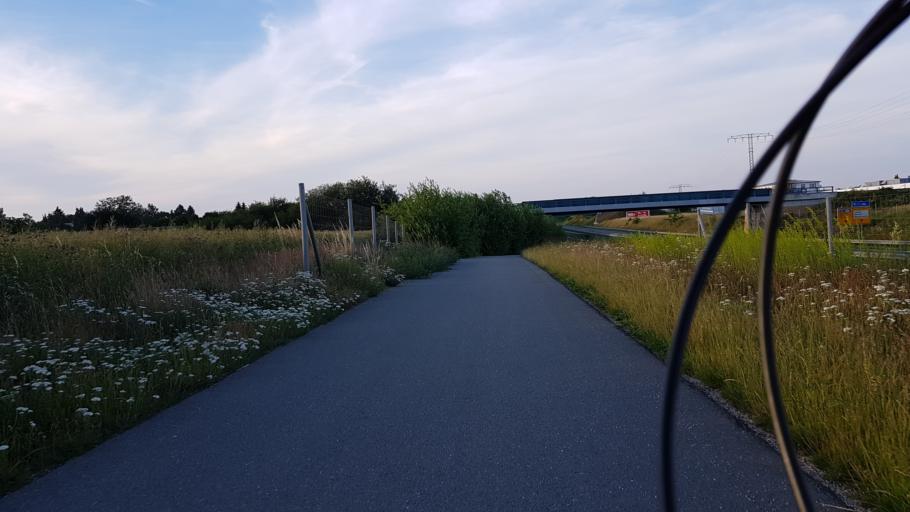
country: DE
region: Mecklenburg-Vorpommern
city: Lankow
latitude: 53.6590
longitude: 11.3541
